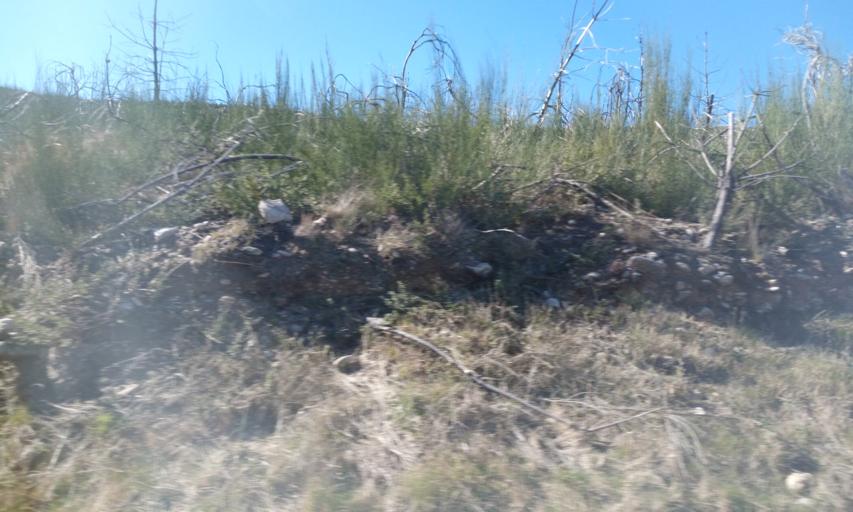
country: PT
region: Guarda
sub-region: Manteigas
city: Manteigas
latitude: 40.4925
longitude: -7.5421
